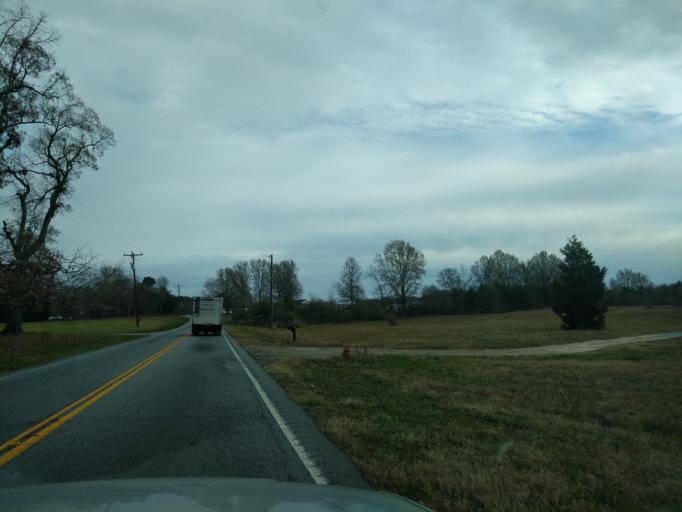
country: US
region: South Carolina
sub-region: Anderson County
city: Williamston
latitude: 34.6616
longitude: -82.5077
